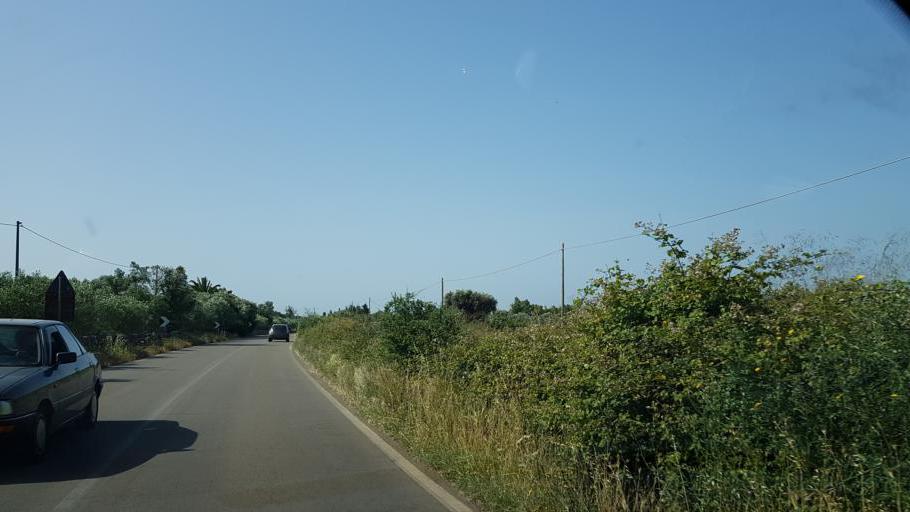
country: IT
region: Apulia
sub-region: Provincia di Lecce
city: Porto Cesareo
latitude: 40.3115
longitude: 17.8631
